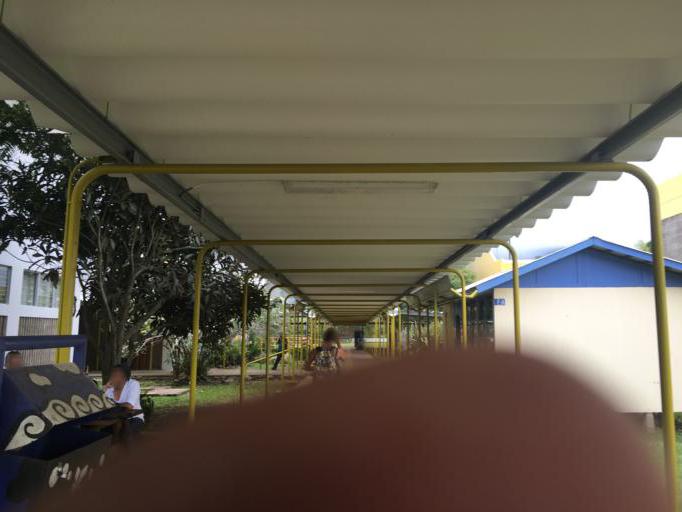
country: CR
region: Cartago
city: Cartago
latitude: 9.8548
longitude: -83.9093
